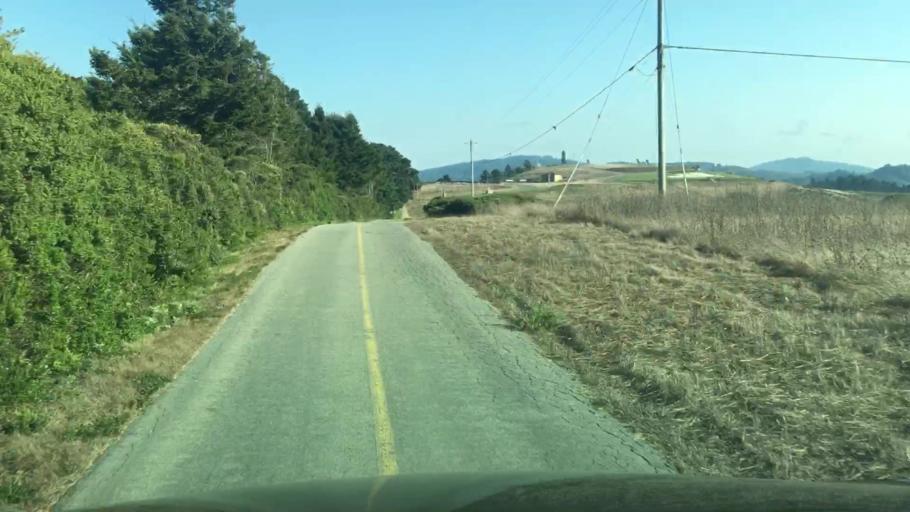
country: US
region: California
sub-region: San Mateo County
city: Highlands-Baywood Park
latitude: 37.5119
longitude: -122.3756
